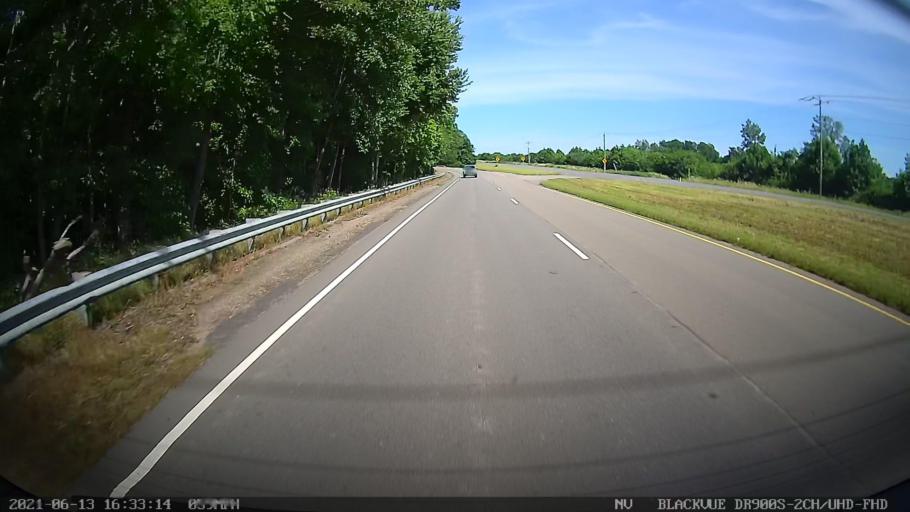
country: US
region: Virginia
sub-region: City of Hopewell
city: Hopewell
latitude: 37.2849
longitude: -77.2453
